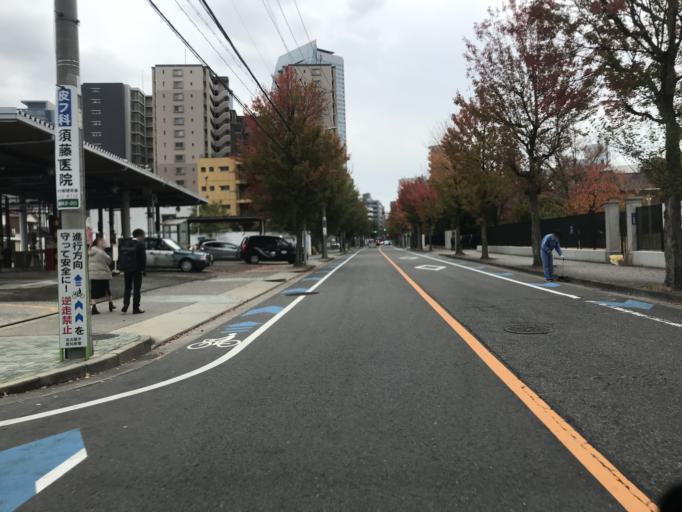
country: JP
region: Aichi
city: Nagoya-shi
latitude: 35.1795
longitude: 136.8820
